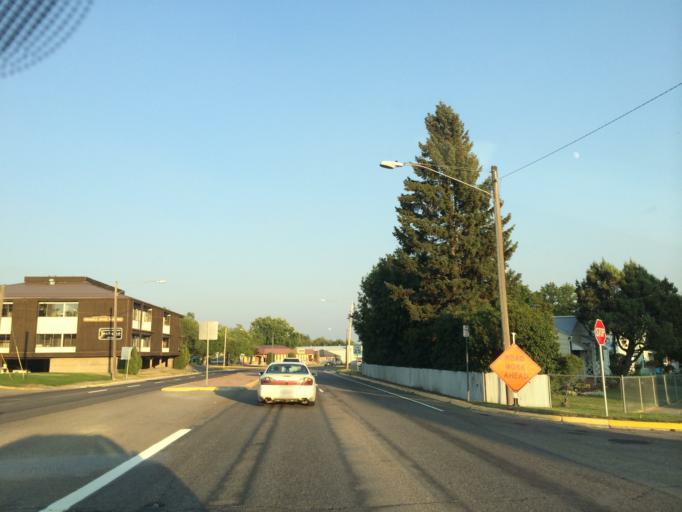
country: US
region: Montana
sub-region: Flathead County
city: Kalispell
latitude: 48.2059
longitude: -114.3182
